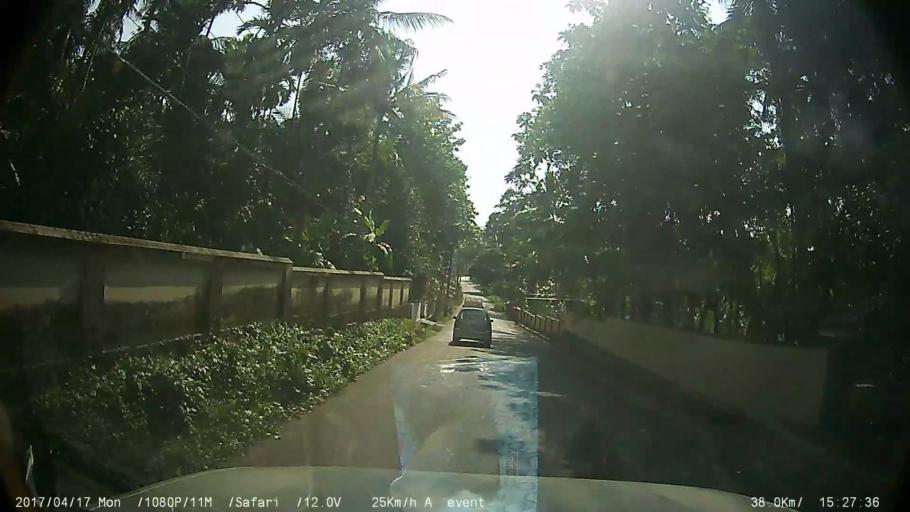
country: IN
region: Kerala
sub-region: Ernakulam
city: Ramamangalam
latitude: 9.9560
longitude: 76.4392
